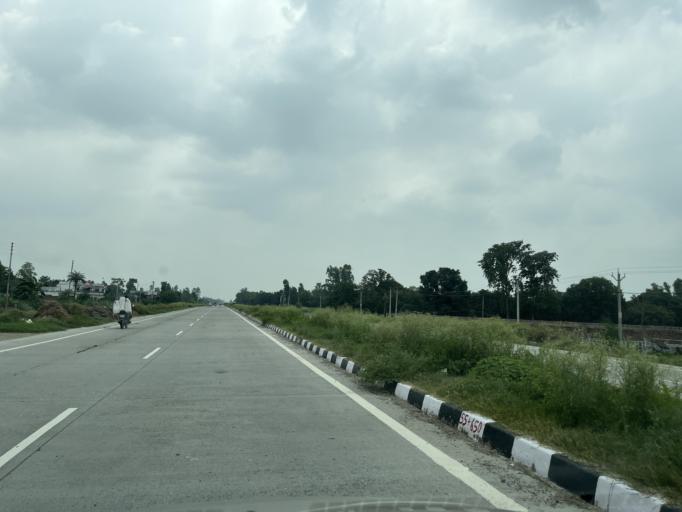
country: IN
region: Uttar Pradesh
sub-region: Bijnor
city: Najibabad
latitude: 29.5487
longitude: 78.3395
